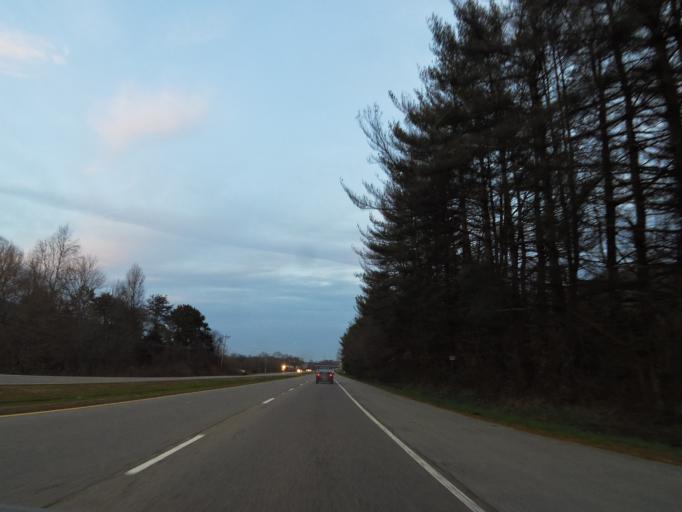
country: US
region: Tennessee
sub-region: Roane County
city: Midtown
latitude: 35.9035
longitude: -84.6008
